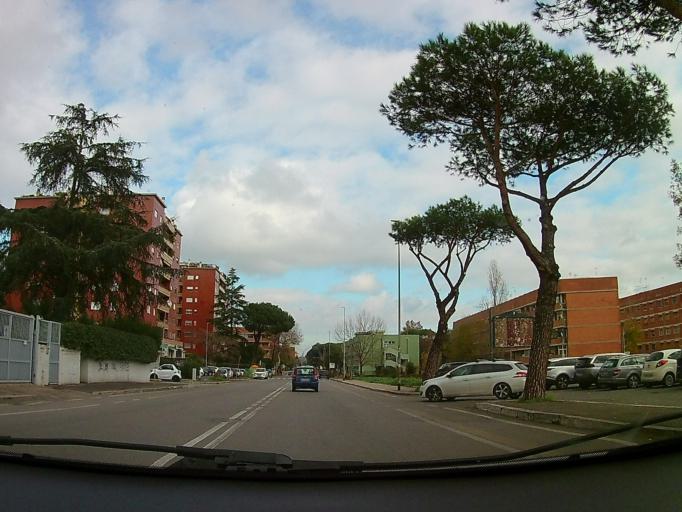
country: IT
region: Latium
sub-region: Citta metropolitana di Roma Capitale
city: Vitinia
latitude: 41.8175
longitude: 12.4391
